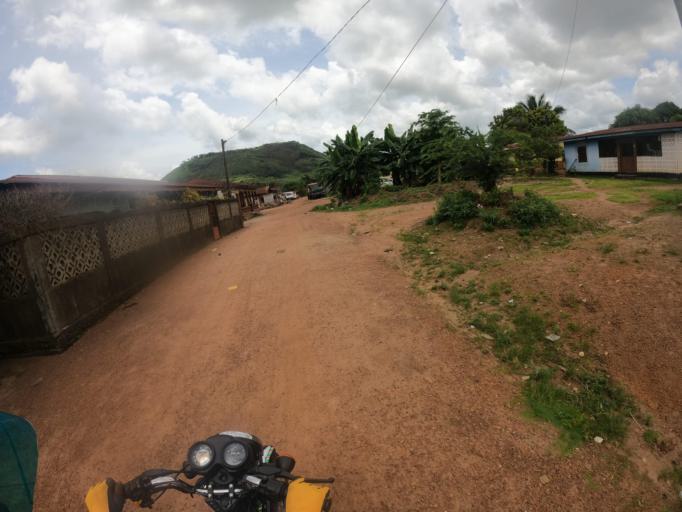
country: SL
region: Northern Province
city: Makeni
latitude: 8.8930
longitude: -12.0502
